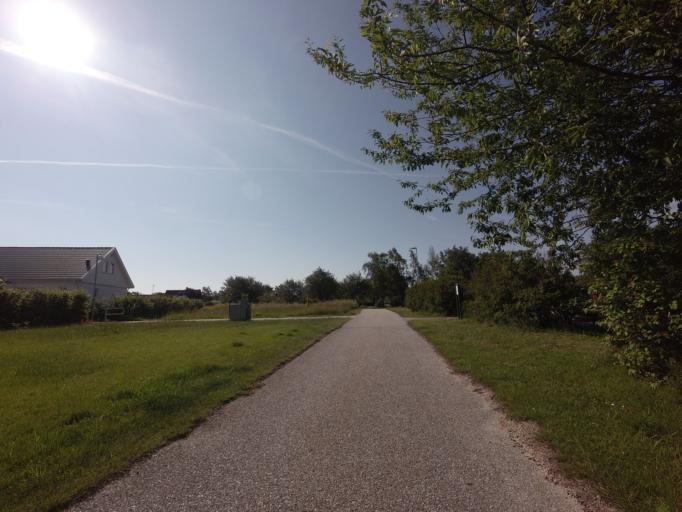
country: SE
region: Skane
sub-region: Malmo
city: Oxie
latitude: 55.4935
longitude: 13.1091
